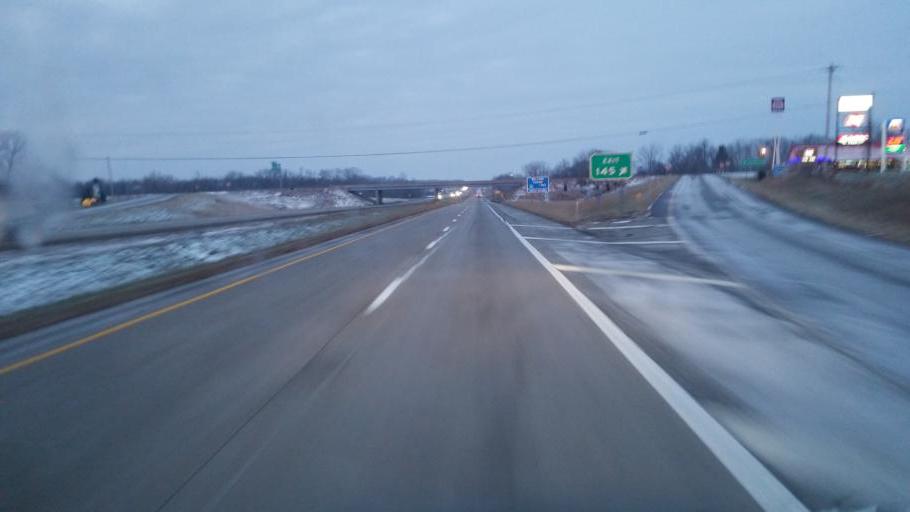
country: US
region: Indiana
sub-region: Wayne County
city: Centerville
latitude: 39.8597
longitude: -84.9930
